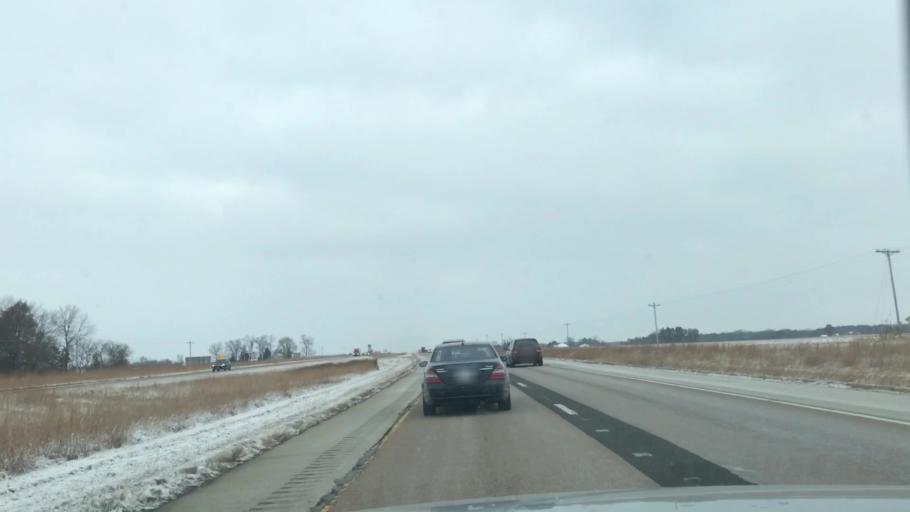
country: US
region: Illinois
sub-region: Montgomery County
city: Litchfield
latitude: 39.2361
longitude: -89.6411
